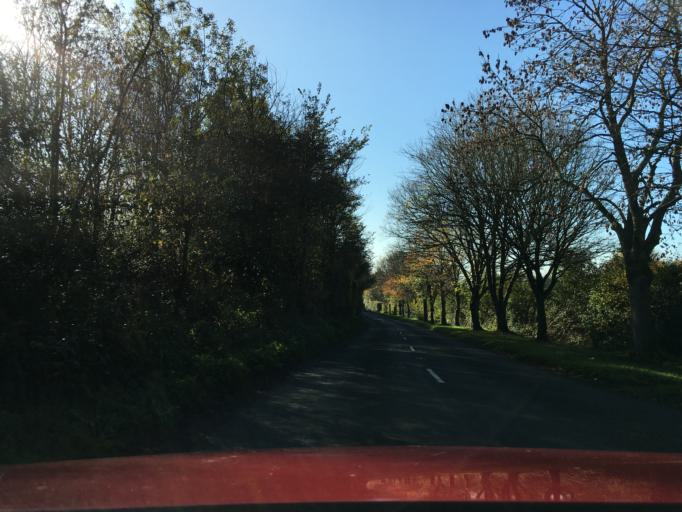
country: GB
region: England
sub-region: Somerset
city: Martock
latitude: 51.0187
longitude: -2.7575
